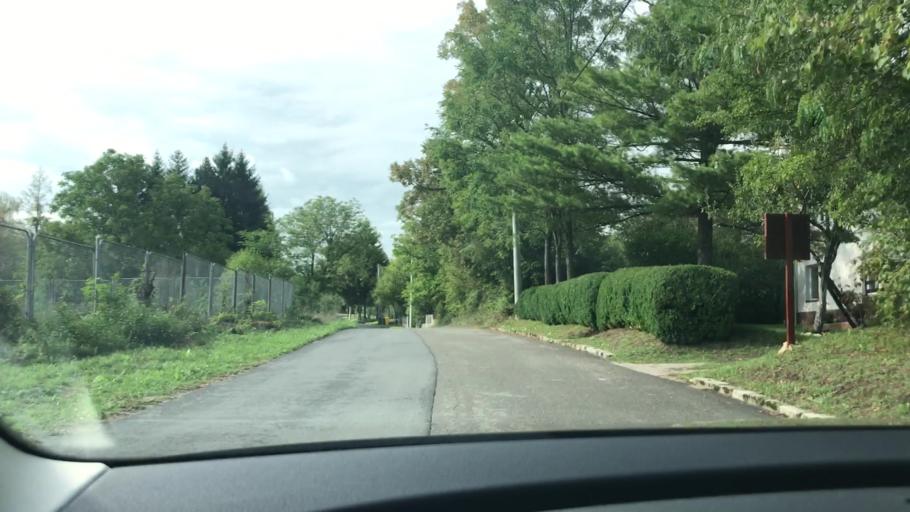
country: BA
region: Federation of Bosnia and Herzegovina
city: Izacic
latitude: 44.8772
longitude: 15.7146
